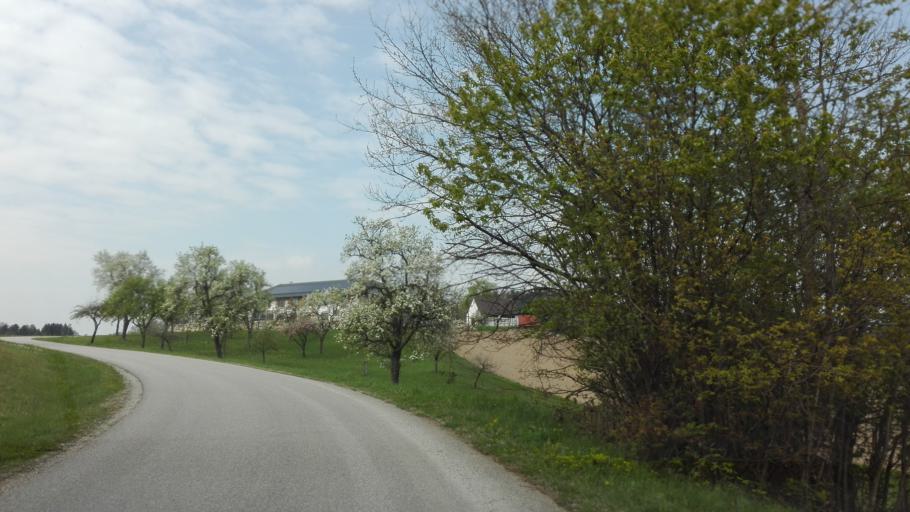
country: AT
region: Upper Austria
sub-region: Politischer Bezirk Perg
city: Bad Kreuzen
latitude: 48.2383
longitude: 14.7376
